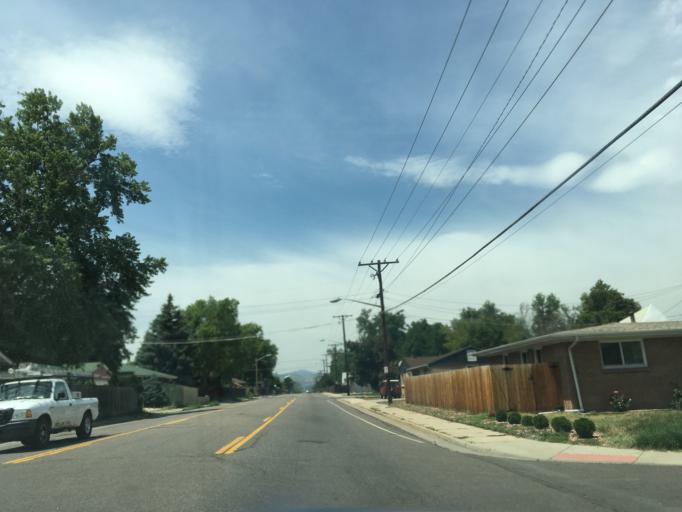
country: US
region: Colorado
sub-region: Arapahoe County
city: Sheridan
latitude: 39.6823
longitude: -105.0381
